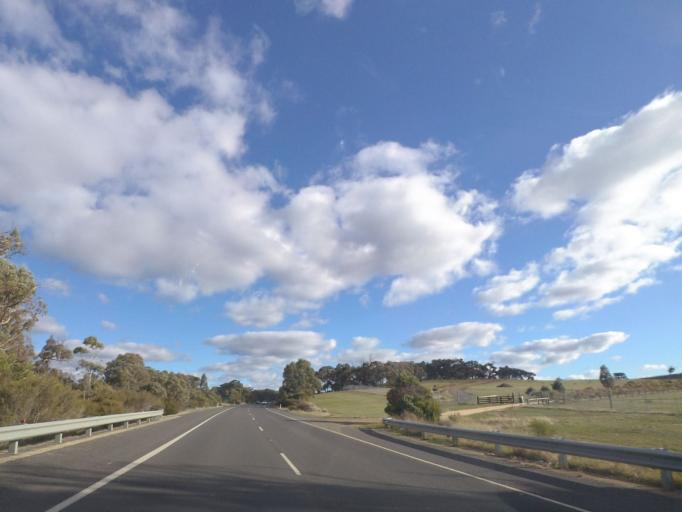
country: AU
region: Victoria
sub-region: Mount Alexander
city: Castlemaine
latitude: -37.0987
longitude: 144.3239
